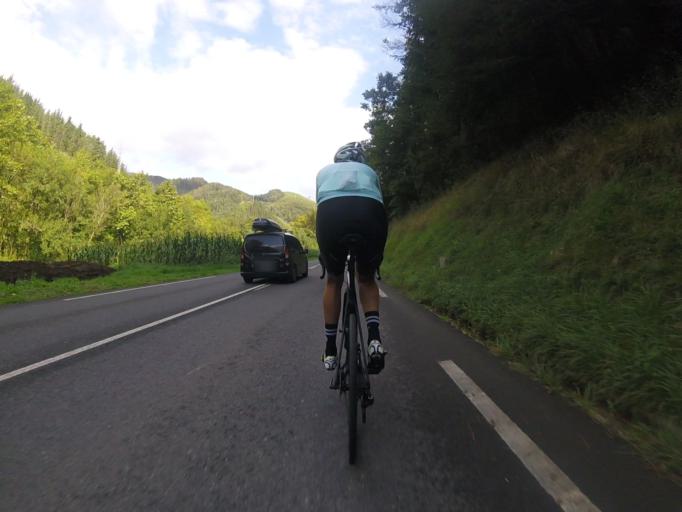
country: ES
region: Basque Country
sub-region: Provincia de Guipuzcoa
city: Alegria de Oria
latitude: 43.0802
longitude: -2.0886
